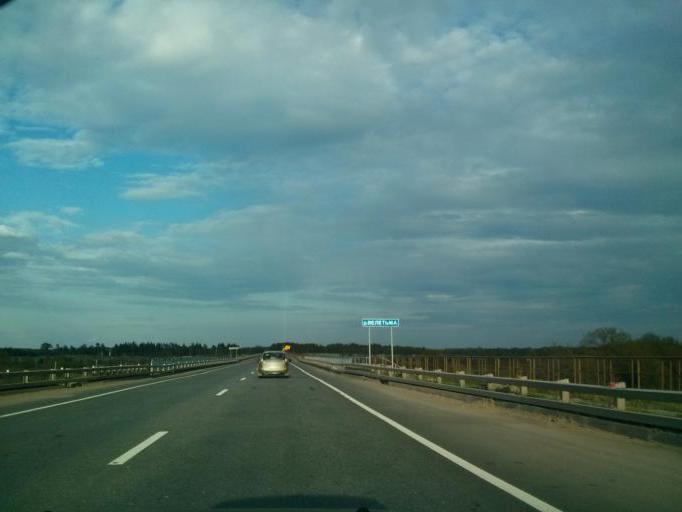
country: RU
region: Nizjnij Novgorod
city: Navashino
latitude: 55.5870
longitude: 42.1340
